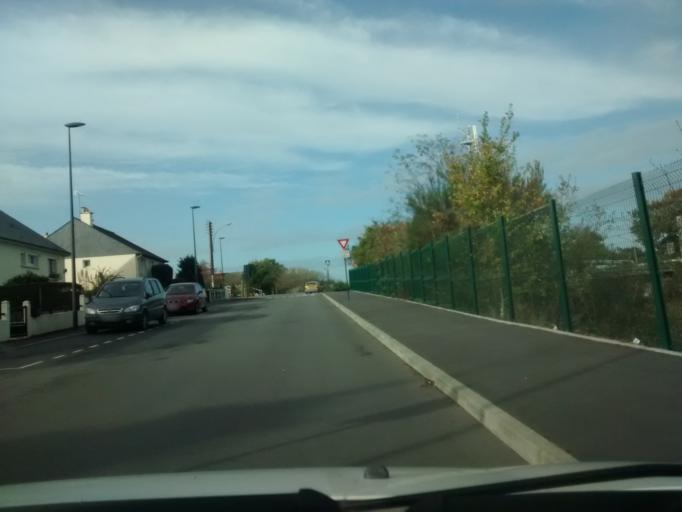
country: FR
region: Brittany
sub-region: Departement d'Ille-et-Vilaine
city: Noyal-sur-Vilaine
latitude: 48.1187
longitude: -1.5307
